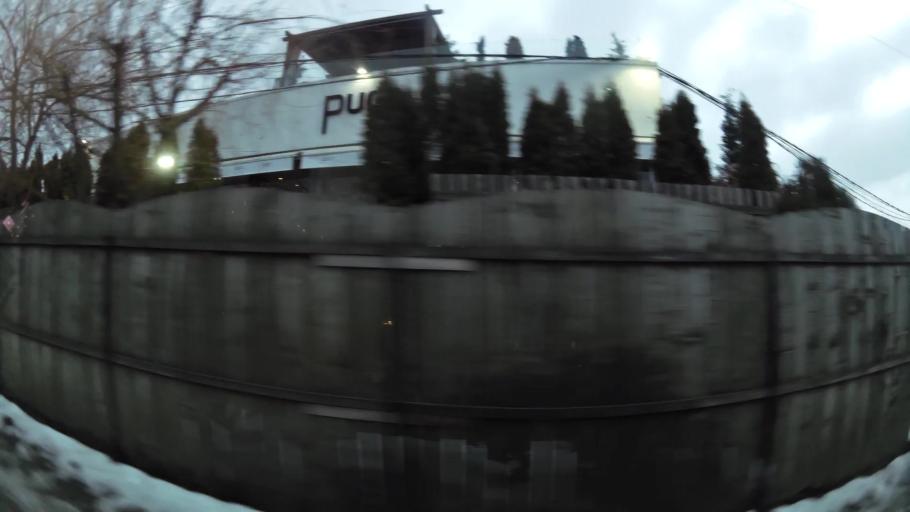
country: XK
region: Pristina
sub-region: Komuna e Prishtines
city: Pristina
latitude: 42.6303
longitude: 21.1620
